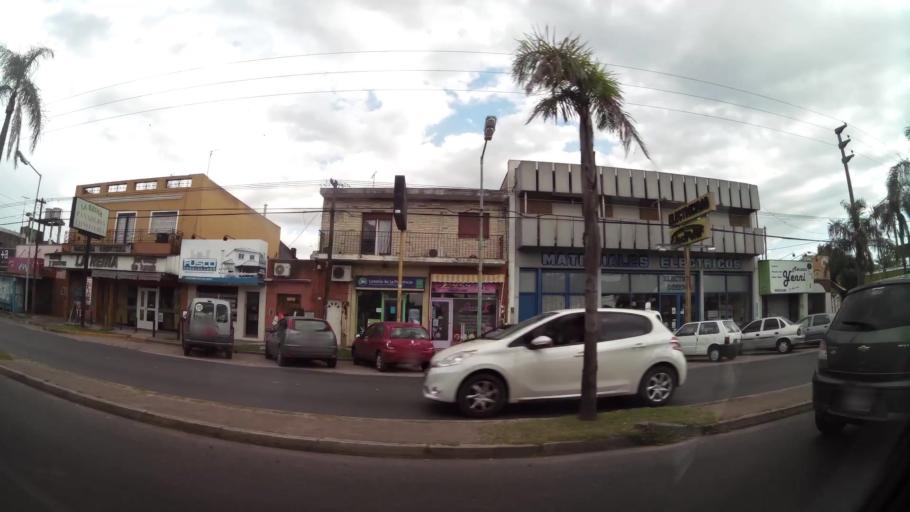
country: AR
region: Buenos Aires
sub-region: Partido de Tigre
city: Tigre
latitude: -34.4665
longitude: -58.6453
